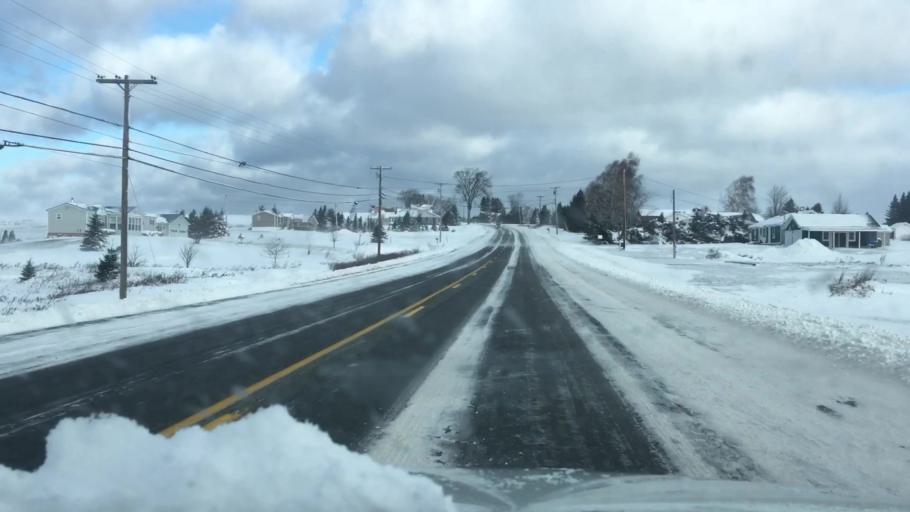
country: US
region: Maine
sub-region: Aroostook County
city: Caribou
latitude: 46.8985
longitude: -68.0155
